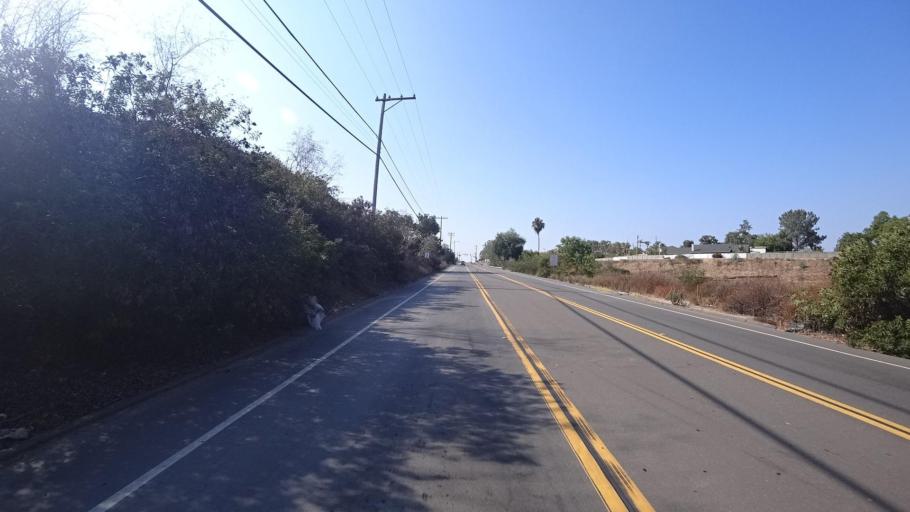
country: US
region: California
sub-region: San Diego County
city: Vista
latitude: 33.2361
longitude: -117.2263
